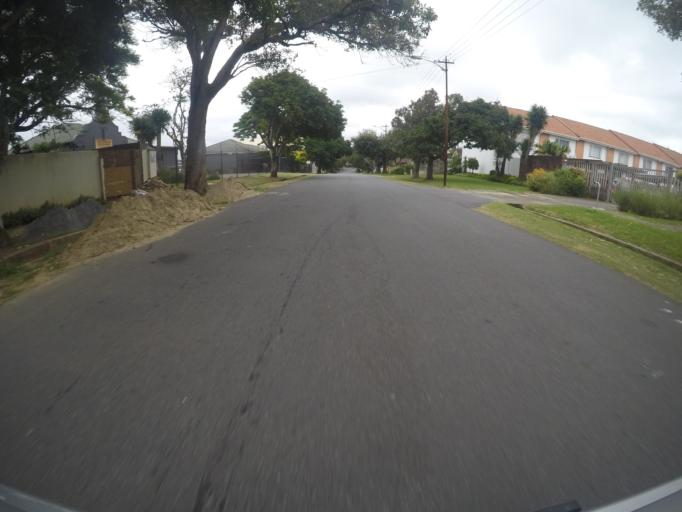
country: ZA
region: Eastern Cape
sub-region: Buffalo City Metropolitan Municipality
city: East London
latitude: -32.9802
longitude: 27.9042
